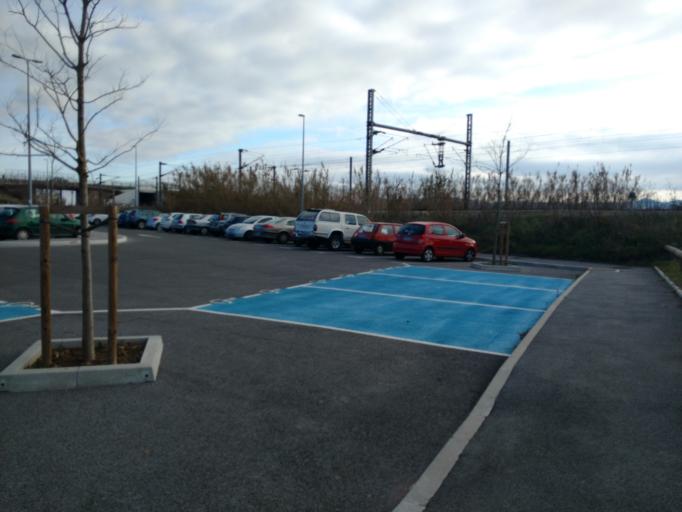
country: FR
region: Provence-Alpes-Cote d'Azur
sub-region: Departement du Var
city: Les Arcs
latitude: 43.4571
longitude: 6.4865
